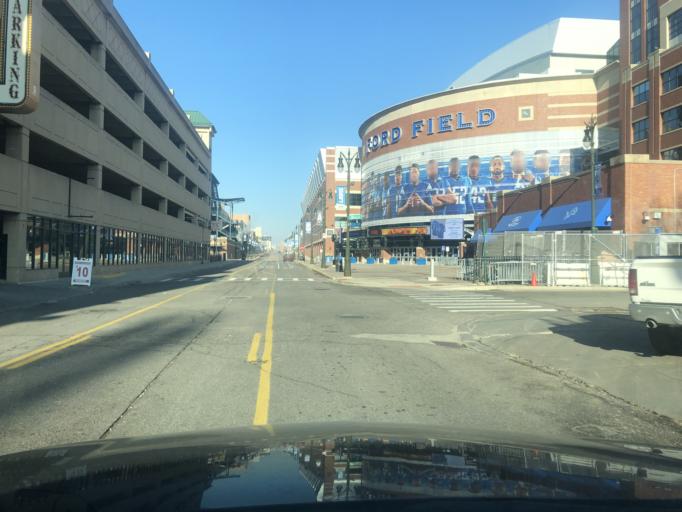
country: US
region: Michigan
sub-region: Wayne County
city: Detroit
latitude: 42.3380
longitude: -83.0461
